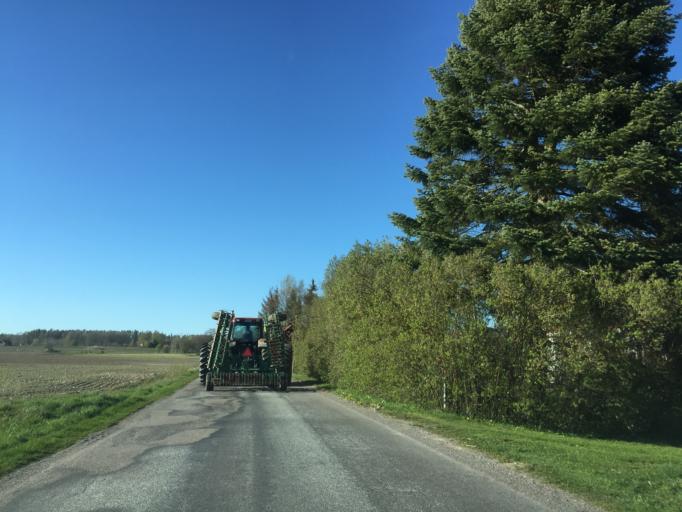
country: SE
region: OErebro
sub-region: Orebro Kommun
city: Odensbacken
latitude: 59.2053
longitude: 15.5503
